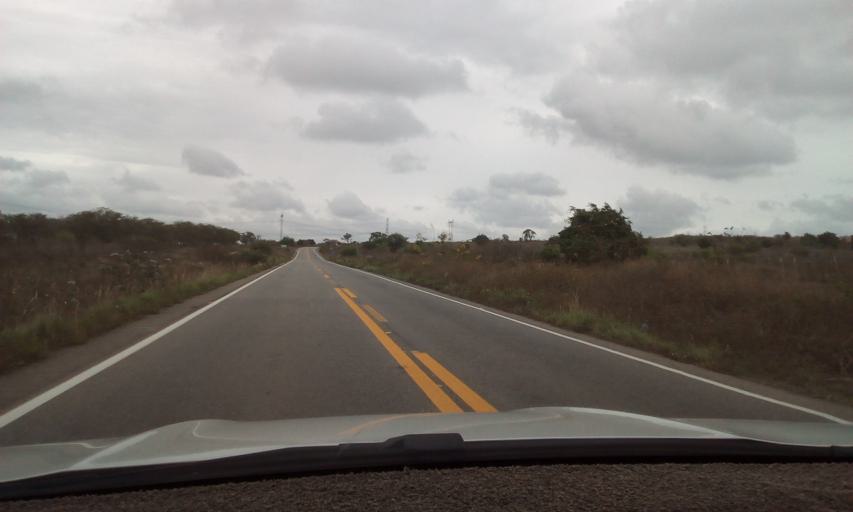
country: BR
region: Paraiba
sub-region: Areia
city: Remigio
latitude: -6.9312
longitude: -35.8351
